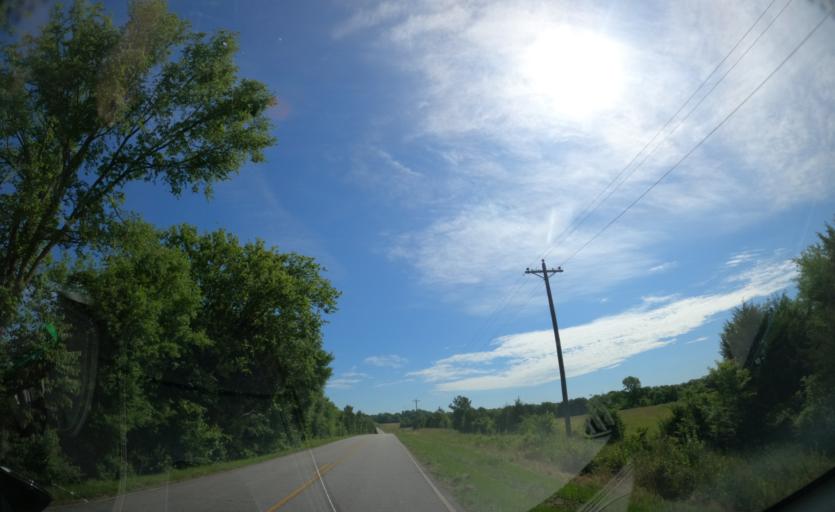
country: US
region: Georgia
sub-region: Elbert County
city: Elberton
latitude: 34.0760
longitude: -82.7407
